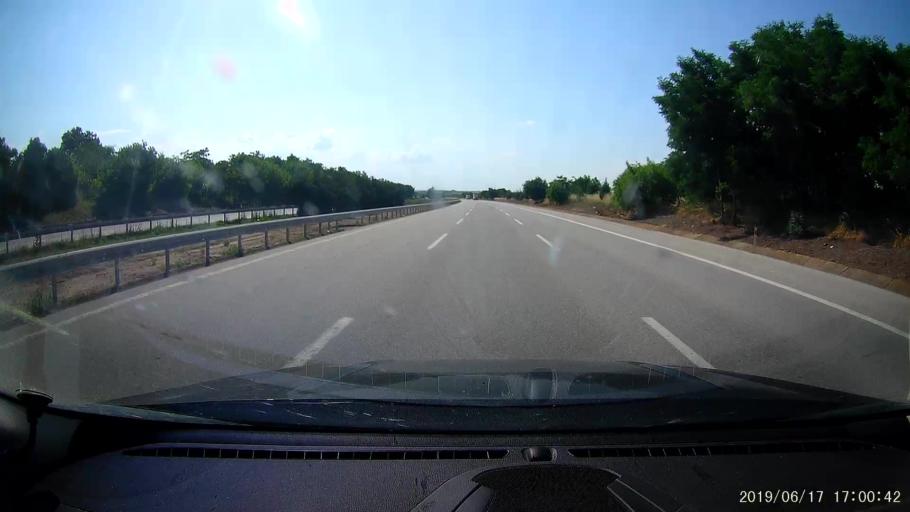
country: TR
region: Edirne
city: Haskoy
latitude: 41.6233
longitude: 26.8239
